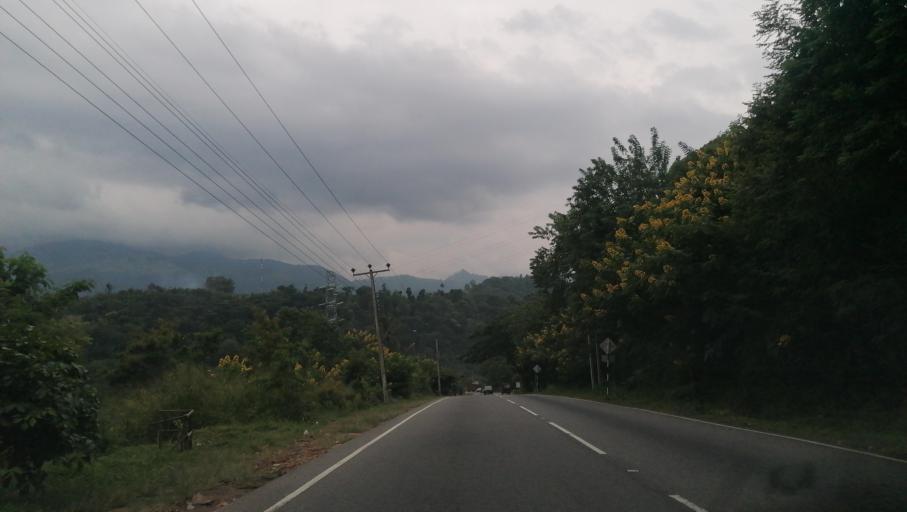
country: LK
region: Central
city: Kandy
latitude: 7.2465
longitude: 80.7311
